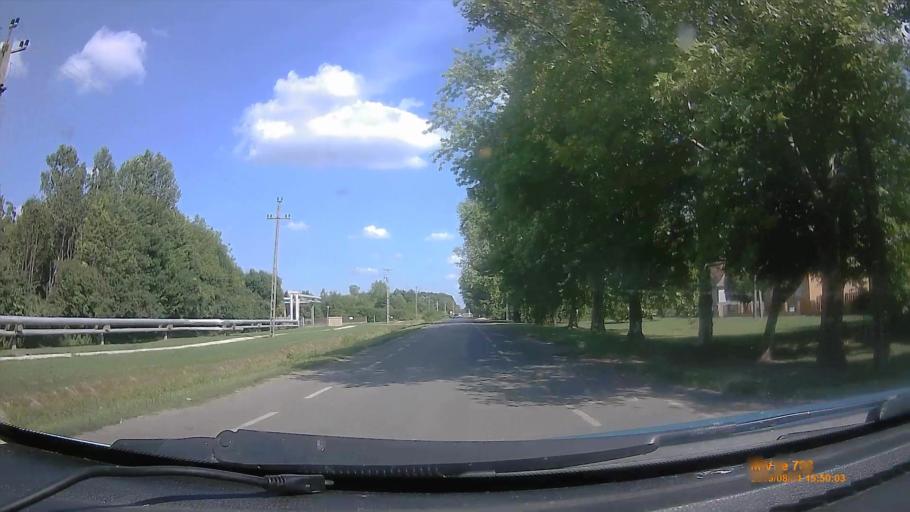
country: HU
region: Baranya
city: Szentlorinc
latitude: 46.0381
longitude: 17.9956
